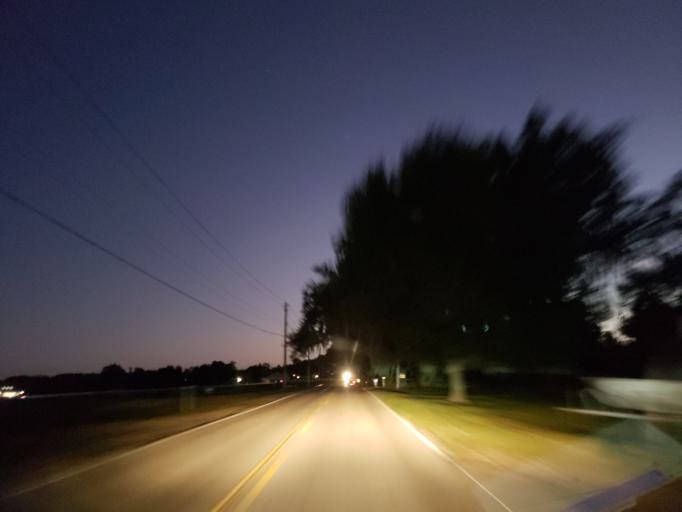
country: US
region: Florida
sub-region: Hillsborough County
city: Dover
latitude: 28.0178
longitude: -82.2241
